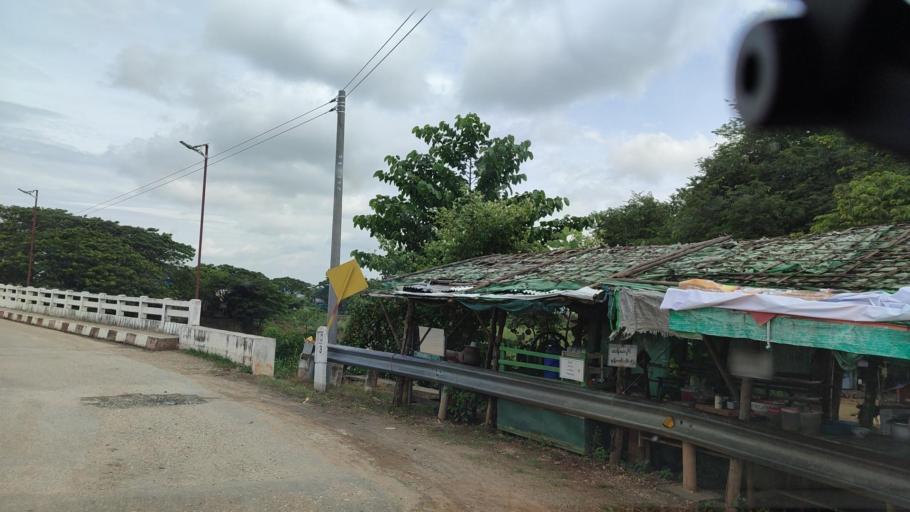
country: MM
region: Bago
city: Pyay
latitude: 18.8371
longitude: 95.2238
